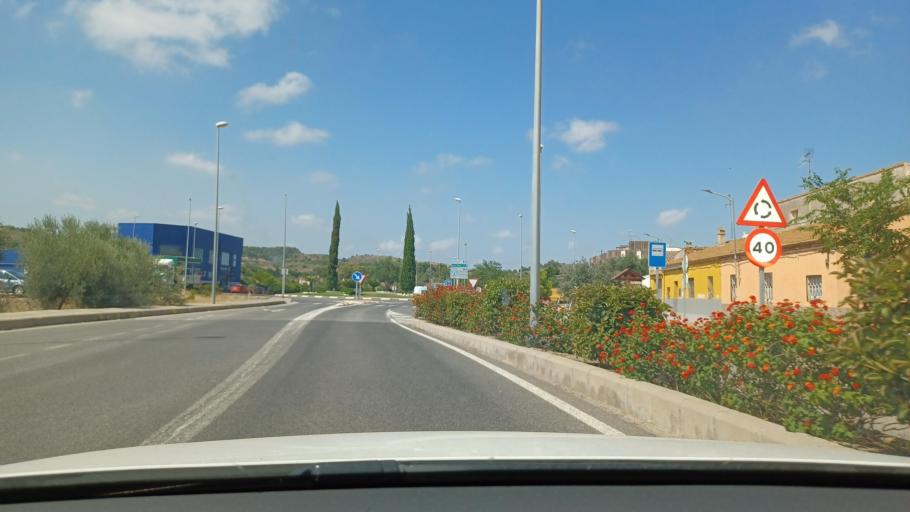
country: ES
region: Valencia
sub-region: Provincia de Castello
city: Almenara
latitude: 39.7690
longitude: -0.2082
